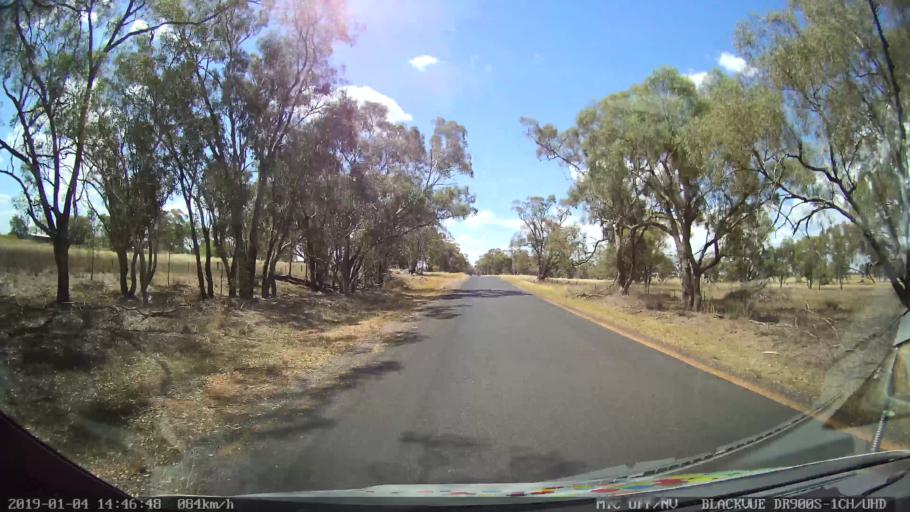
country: AU
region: New South Wales
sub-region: Dubbo Municipality
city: Dubbo
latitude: -32.0770
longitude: 148.6590
